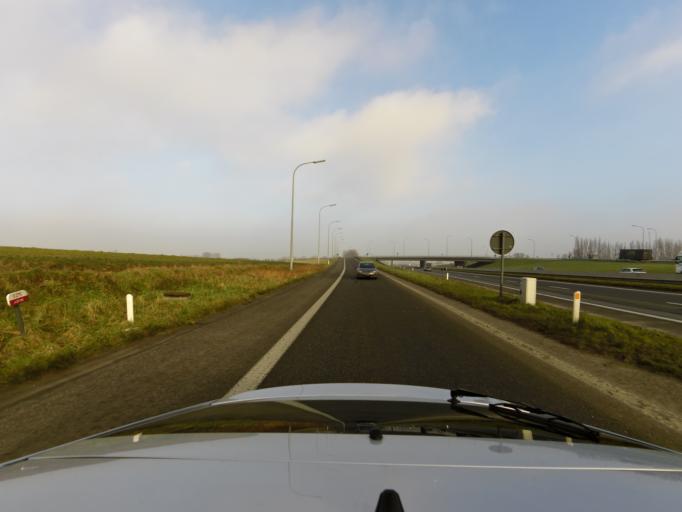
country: BE
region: Flanders
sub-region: Provincie West-Vlaanderen
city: Lichtervelde
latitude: 51.0073
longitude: 3.1712
